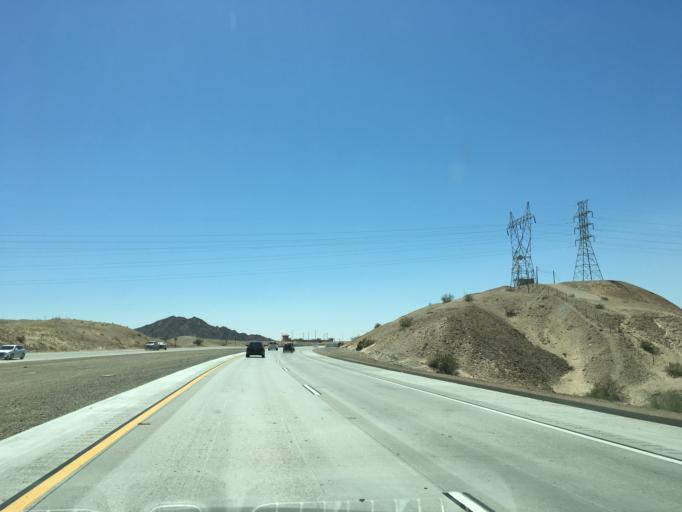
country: MX
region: Baja California
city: Los Algodones
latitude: 32.7436
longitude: -114.7111
